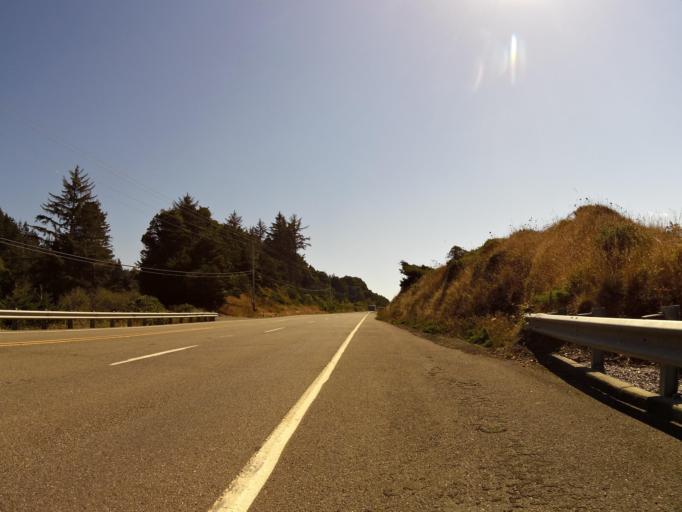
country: US
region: Oregon
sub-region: Curry County
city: Port Orford
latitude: 42.7079
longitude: -124.4605
